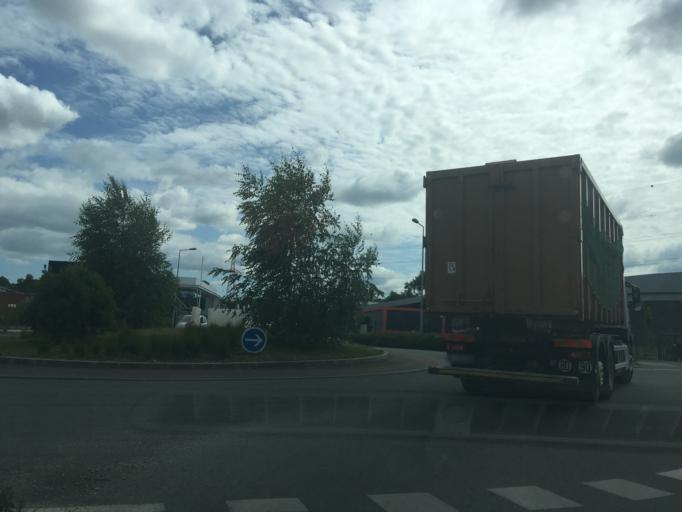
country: FR
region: Aquitaine
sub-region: Departement de la Gironde
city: Le Haillan
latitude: 44.8716
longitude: -0.6612
